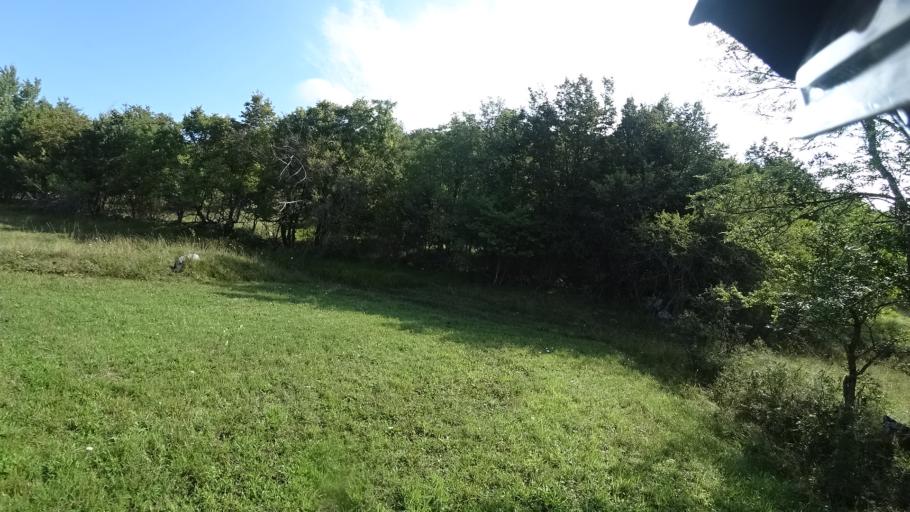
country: HR
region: Zadarska
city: Gracac
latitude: 44.3312
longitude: 15.9650
